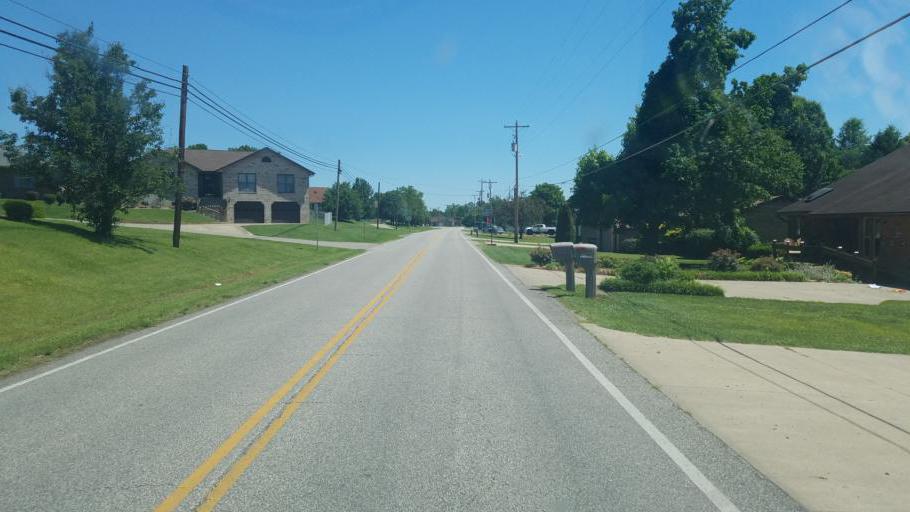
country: US
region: West Virginia
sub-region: Cabell County
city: Pea Ridge
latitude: 38.4538
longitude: -82.3255
